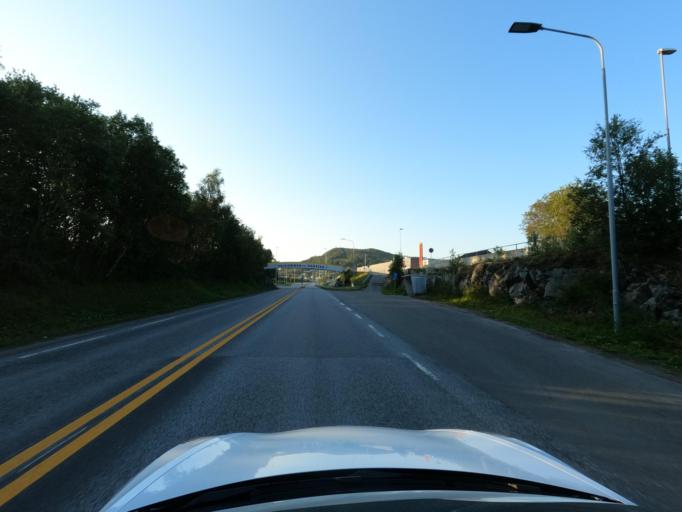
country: NO
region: Troms
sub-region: Harstad
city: Harstad
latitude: 68.7780
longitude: 16.5637
